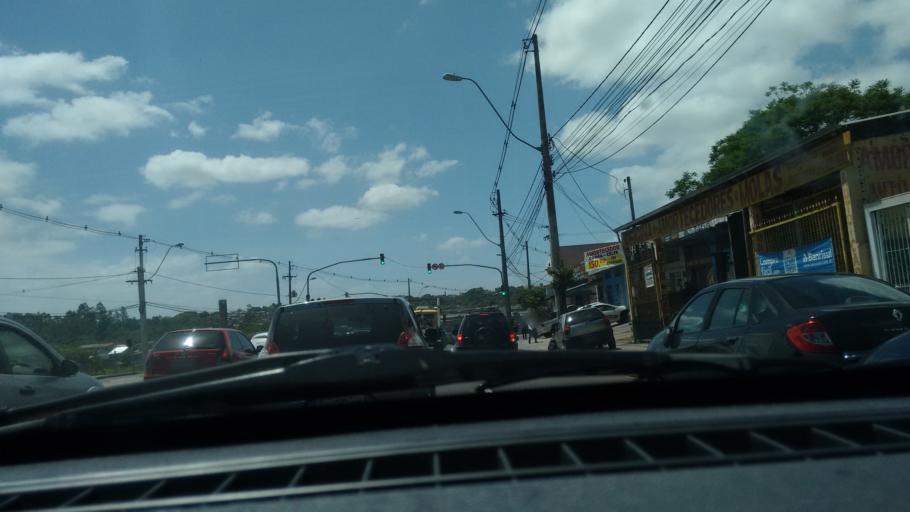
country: BR
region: Rio Grande do Sul
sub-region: Cachoeirinha
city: Cachoeirinha
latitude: -30.0117
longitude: -51.1279
